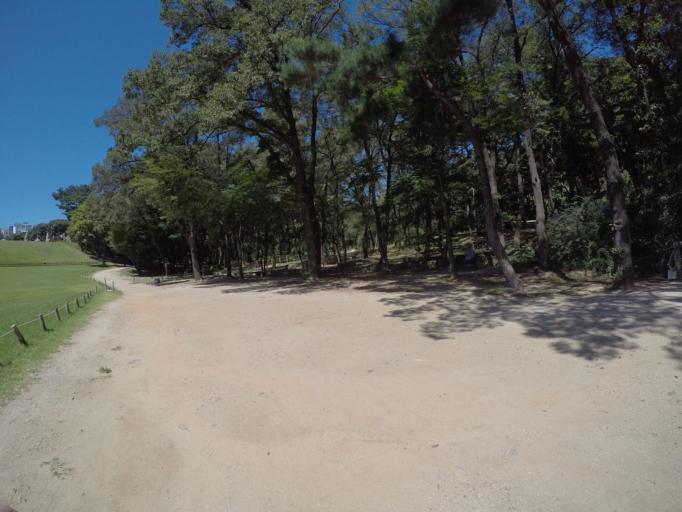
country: KR
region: Seoul
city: Seoul
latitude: 37.5084
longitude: 127.0465
